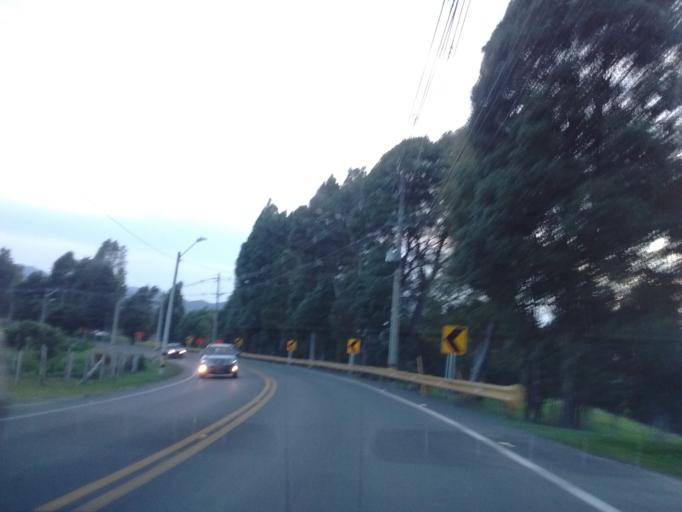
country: CO
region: Antioquia
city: Envigado
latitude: 6.1632
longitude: -75.5146
